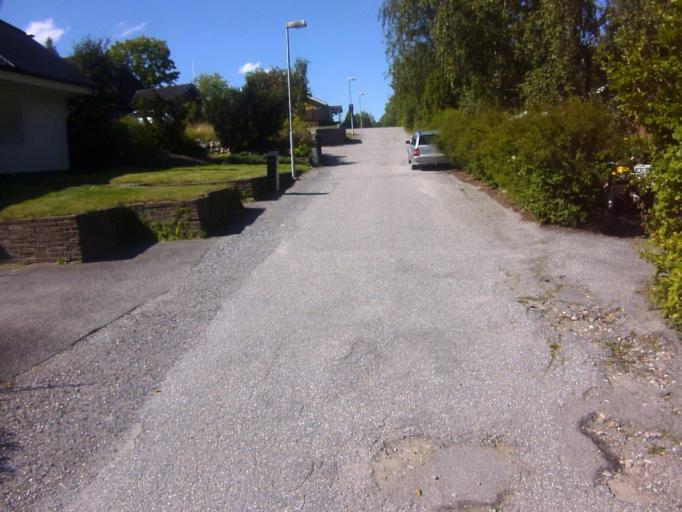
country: SE
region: Soedermanland
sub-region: Eskilstuna Kommun
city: Hallbybrunn
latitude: 59.3735
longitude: 16.4443
